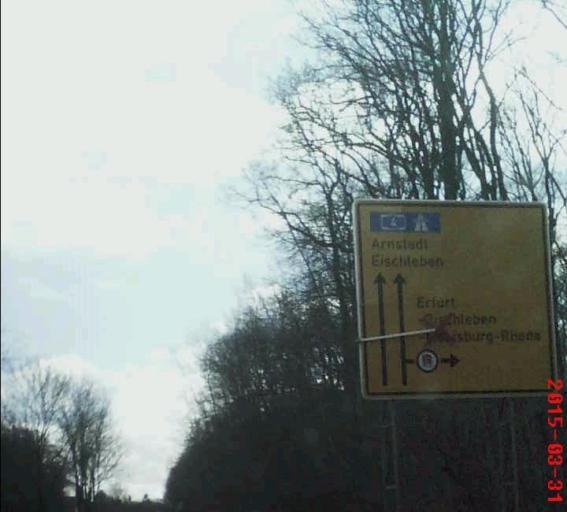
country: DE
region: Thuringia
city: Erfurt
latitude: 50.9460
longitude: 11.0300
